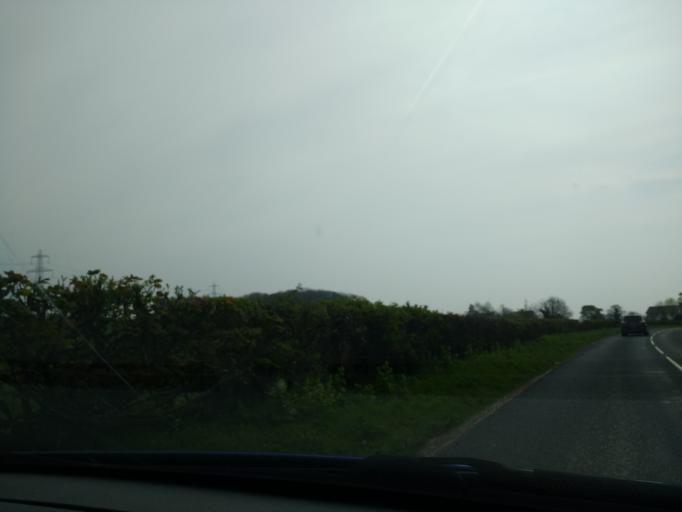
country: GB
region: England
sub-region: Lancashire
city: Lancaster
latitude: 54.0148
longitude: -2.8128
